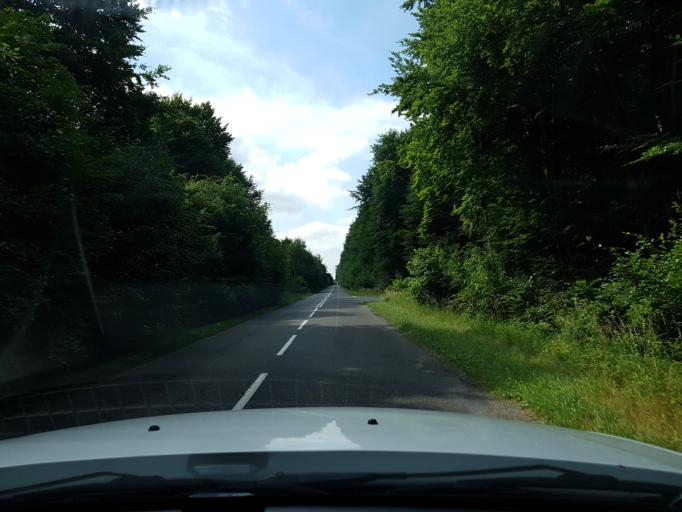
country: PL
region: West Pomeranian Voivodeship
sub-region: Powiat gryfinski
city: Banie
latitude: 53.0097
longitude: 14.7223
